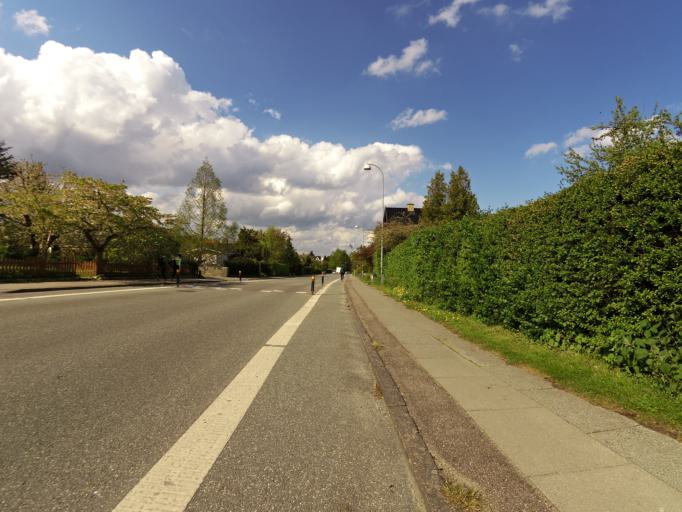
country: DK
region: Capital Region
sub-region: Gladsaxe Municipality
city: Buddinge
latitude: 55.7239
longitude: 12.5107
